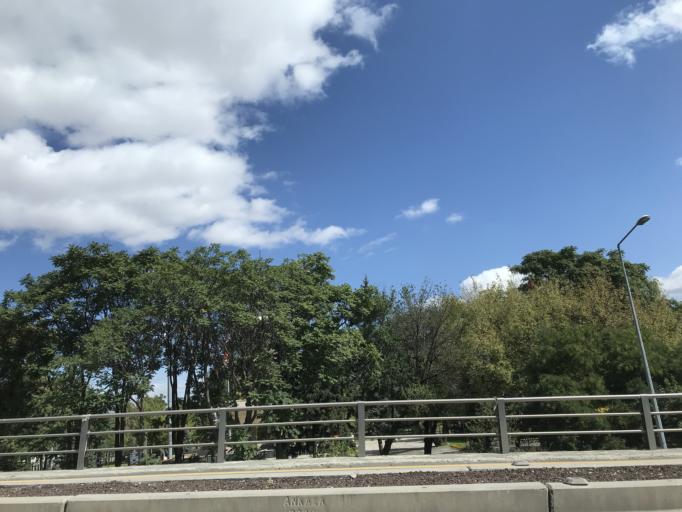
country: TR
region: Ankara
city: Ankara
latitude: 39.9384
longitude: 32.8412
